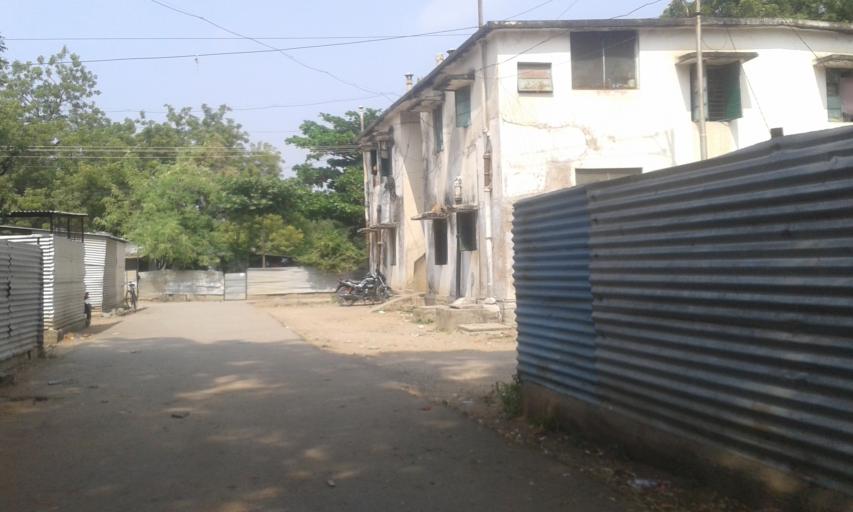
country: IN
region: Karnataka
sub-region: Raichur
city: Lingsugur
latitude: 16.1926
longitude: 76.6618
